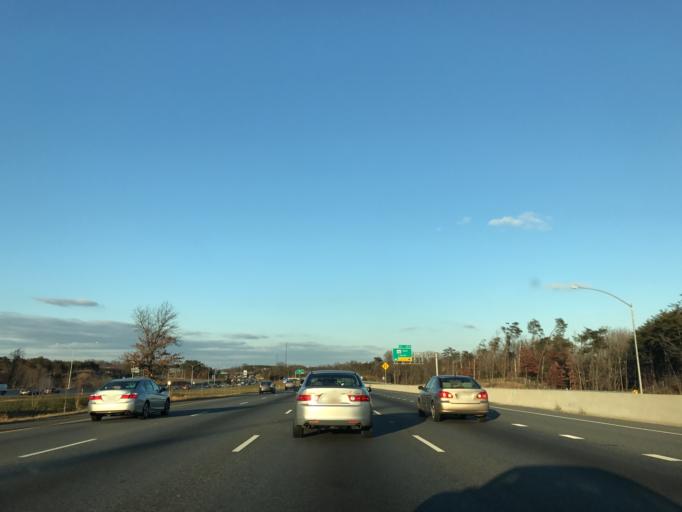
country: US
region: Maryland
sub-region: Prince George's County
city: West Laurel
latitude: 39.0862
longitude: -76.8958
